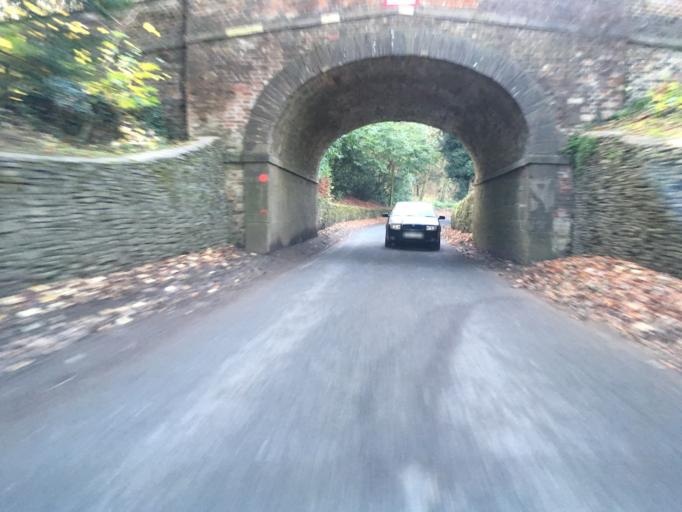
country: GB
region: England
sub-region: Wiltshire
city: Luckington
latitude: 51.5430
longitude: -2.2884
